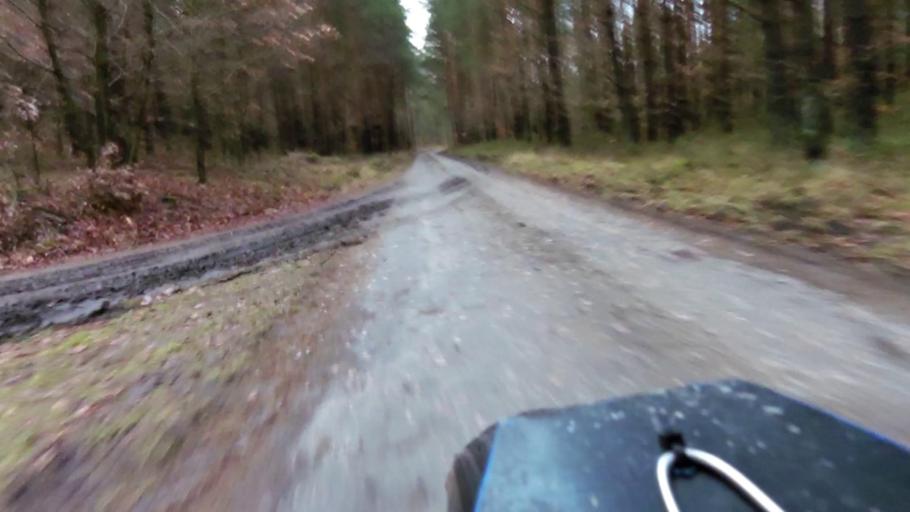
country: PL
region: Lubusz
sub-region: Powiat gorzowski
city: Bogdaniec
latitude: 52.6935
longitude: 15.0034
